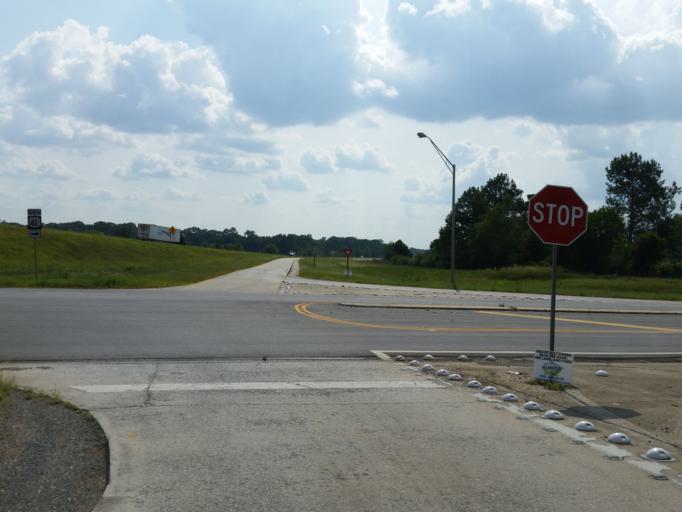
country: US
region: Georgia
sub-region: Crisp County
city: Cordele
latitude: 31.9239
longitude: -83.7718
